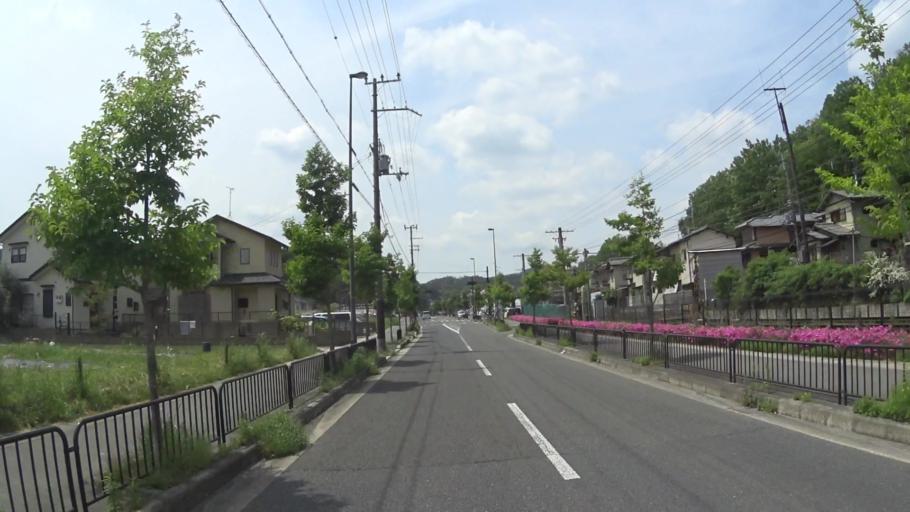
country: JP
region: Kyoto
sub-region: Kyoto-shi
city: Kamigyo-ku
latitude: 35.0711
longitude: 135.7719
